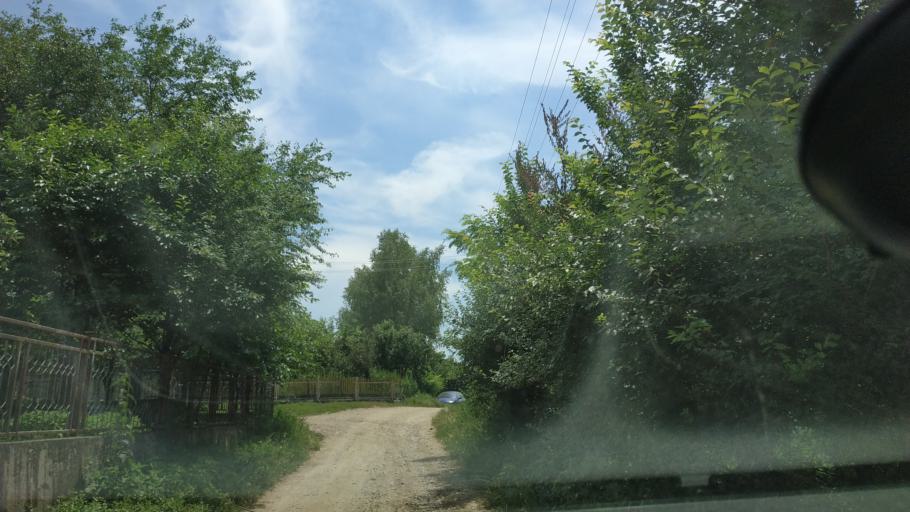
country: RS
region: Central Serbia
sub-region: Nisavski Okrug
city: Aleksinac
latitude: 43.5779
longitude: 21.7011
